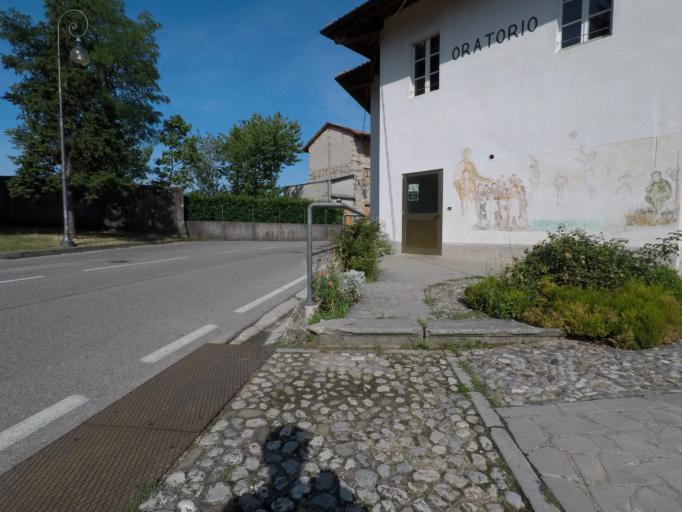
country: IT
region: Friuli Venezia Giulia
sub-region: Provincia di Udine
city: Colloredo di Prato
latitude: 46.0501
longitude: 13.1427
